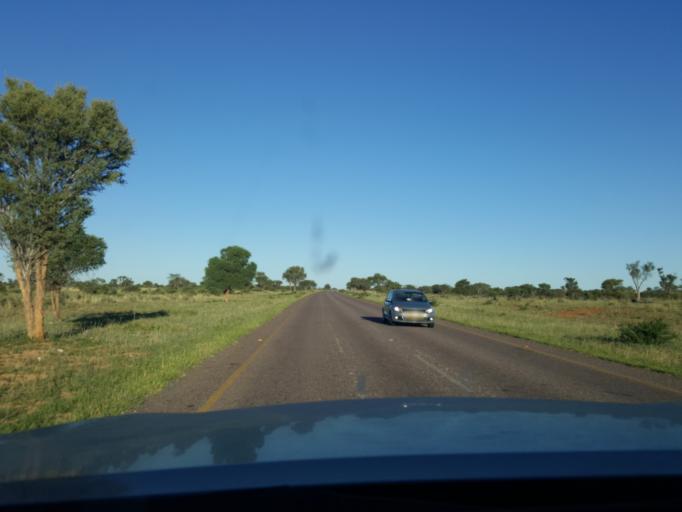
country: BW
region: Southern
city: Khakhea
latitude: -24.3065
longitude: 23.4053
